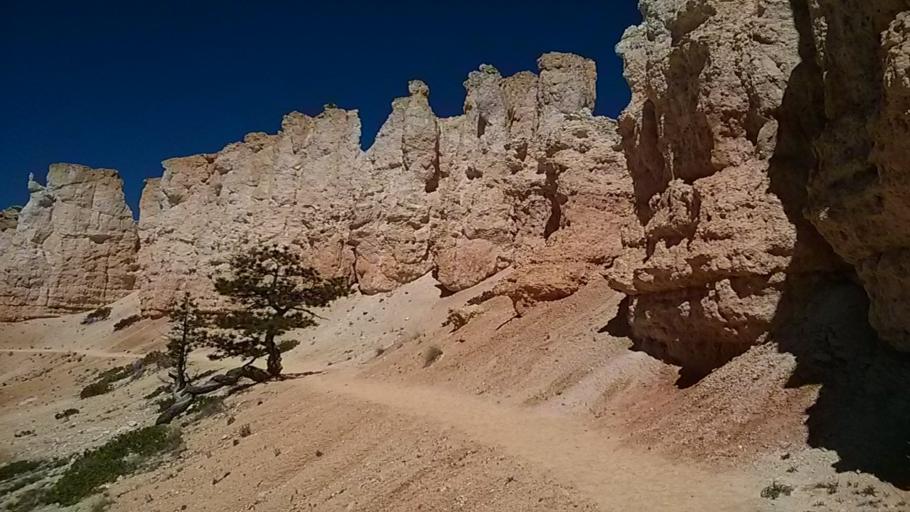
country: US
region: Utah
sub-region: Garfield County
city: Panguitch
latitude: 37.6361
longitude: -112.1529
